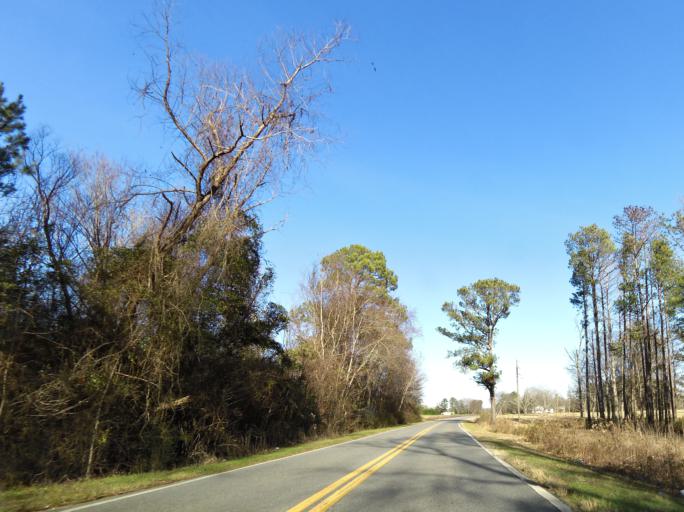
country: US
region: Georgia
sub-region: Bibb County
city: West Point
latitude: 32.7723
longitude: -83.8309
